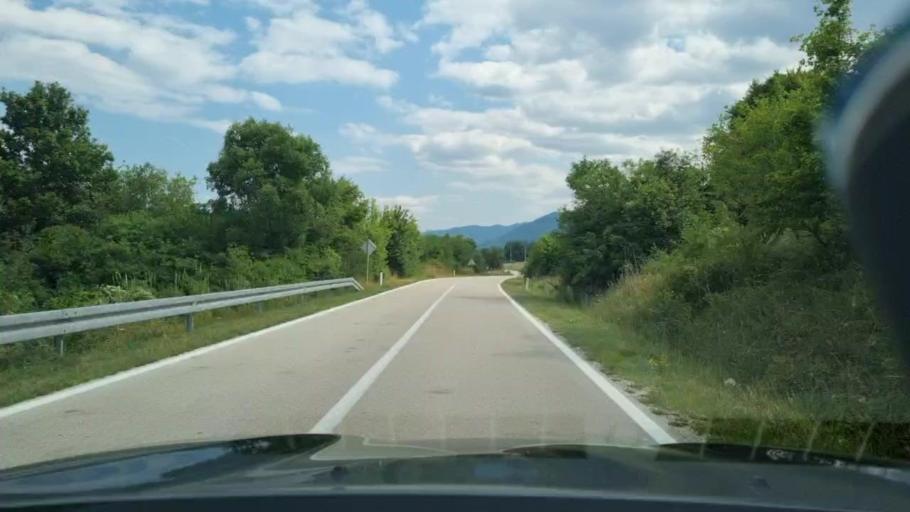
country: BA
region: Federation of Bosnia and Herzegovina
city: Bosansko Grahovo
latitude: 44.0507
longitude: 16.5873
